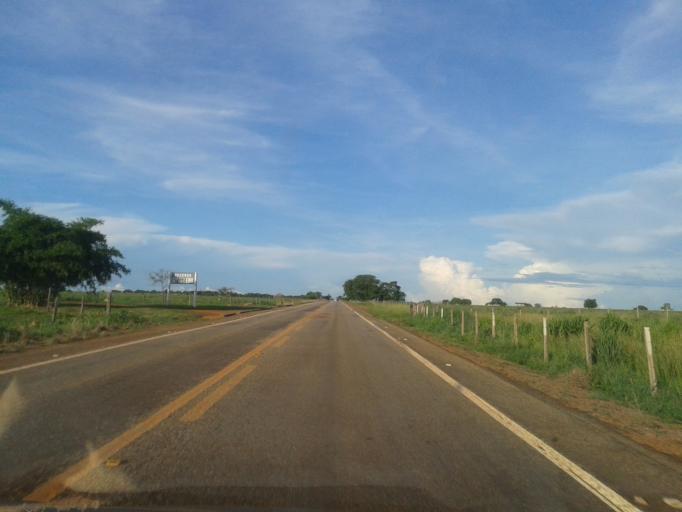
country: BR
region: Goias
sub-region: Sao Miguel Do Araguaia
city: Sao Miguel do Araguaia
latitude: -13.4366
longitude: -50.2855
